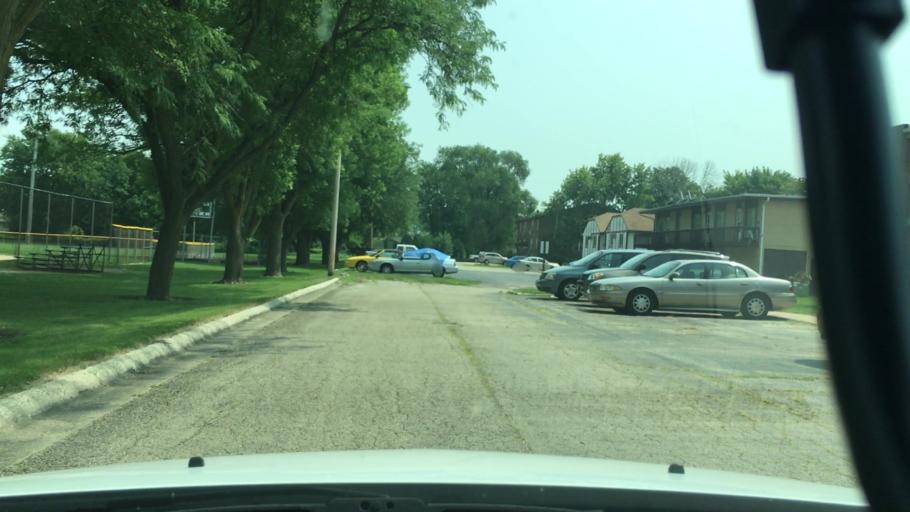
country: US
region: Illinois
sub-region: Ogle County
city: Rochelle
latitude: 41.9266
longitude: -89.0608
